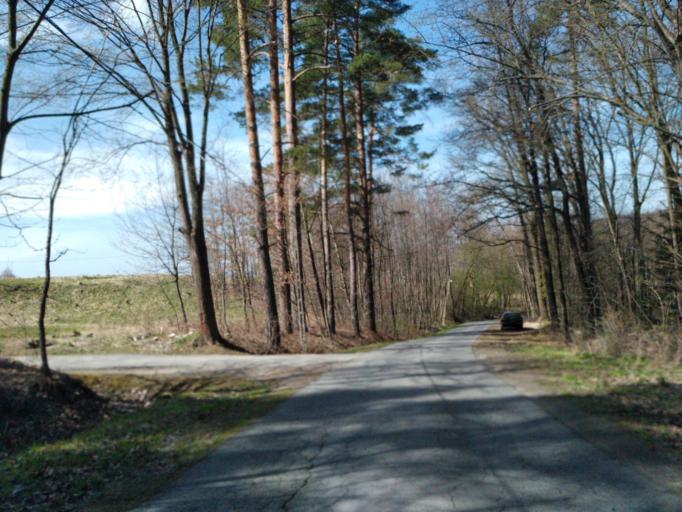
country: PL
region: Subcarpathian Voivodeship
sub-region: Powiat strzyzowski
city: Polomia
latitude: 49.9243
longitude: 21.8877
